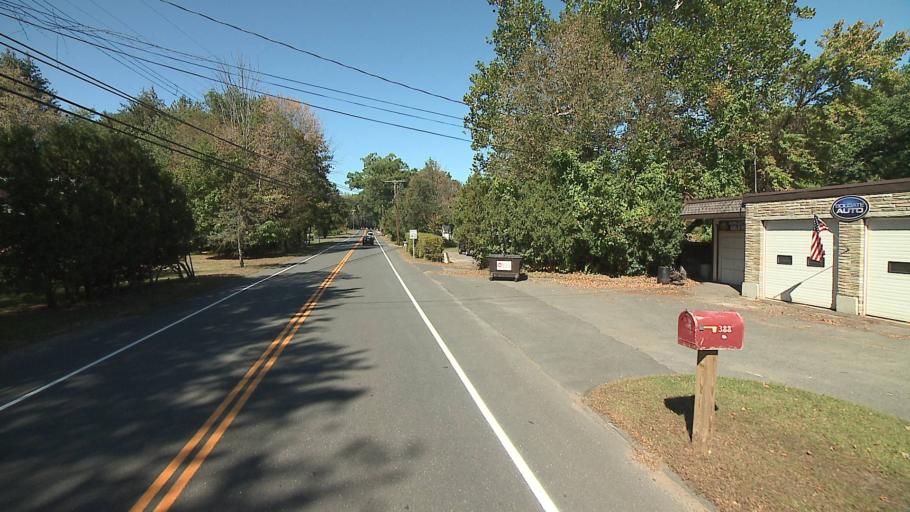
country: US
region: Connecticut
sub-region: Hartford County
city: Salmon Brook
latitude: 41.9698
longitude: -72.7952
